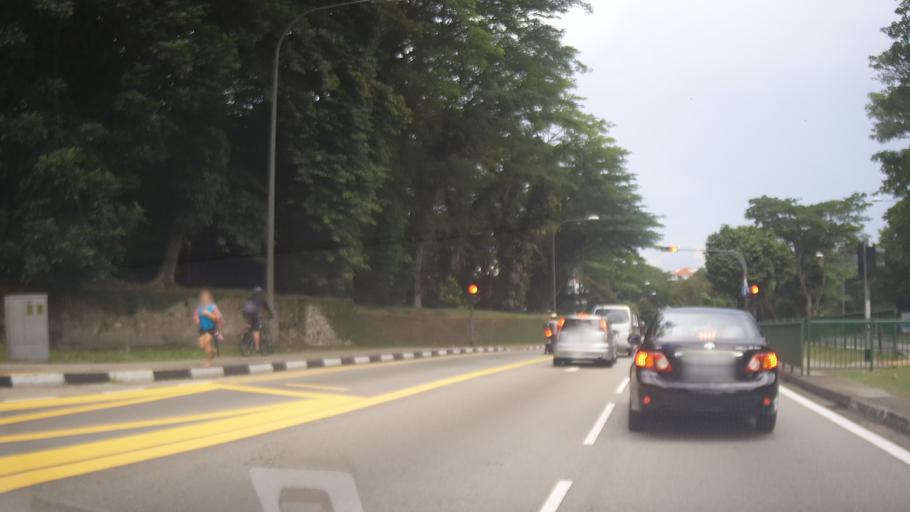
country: SG
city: Singapore
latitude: 1.3520
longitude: 103.7699
